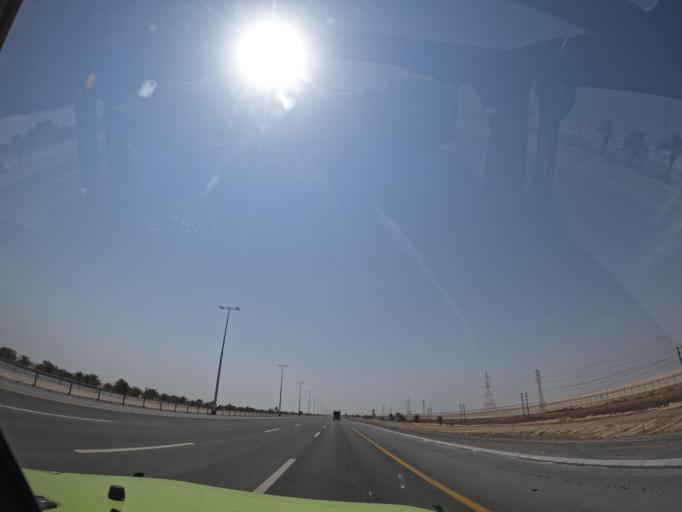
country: AE
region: Abu Dhabi
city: Abu Dhabi
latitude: 24.2062
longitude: 54.4035
